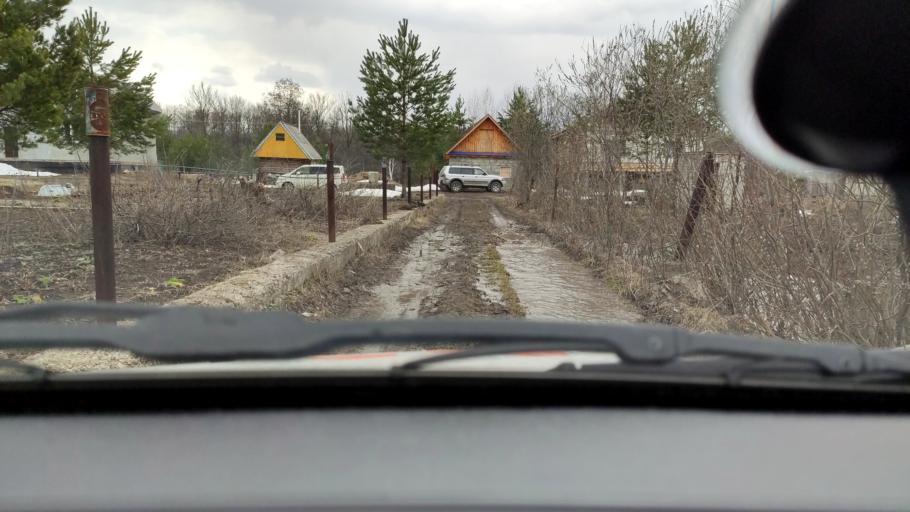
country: RU
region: Bashkortostan
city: Iglino
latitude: 54.8424
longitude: 56.2194
